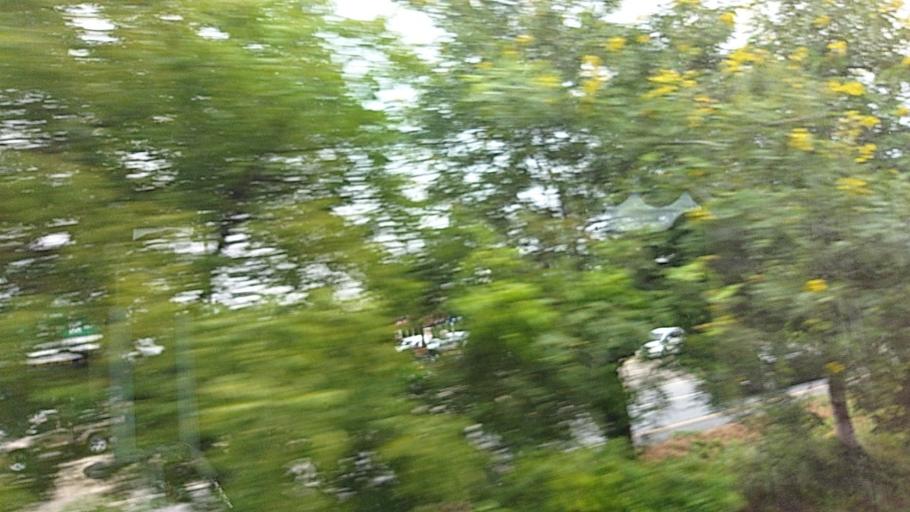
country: TH
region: Nakhon Ratchasima
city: Non Sung
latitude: 15.0987
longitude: 102.2820
